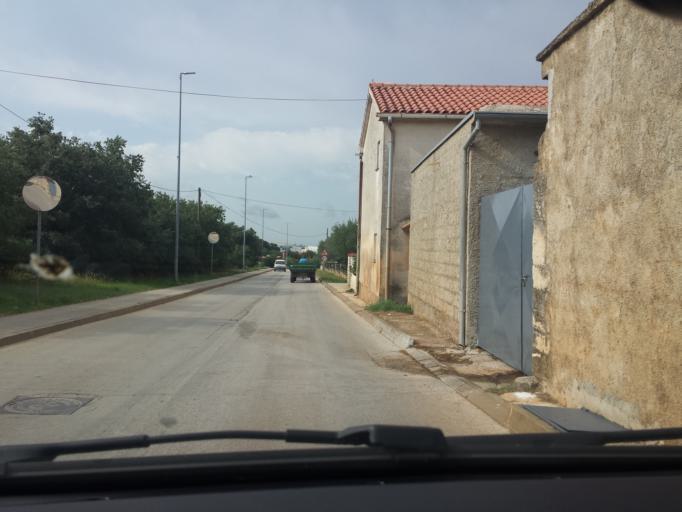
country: HR
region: Istarska
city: Galizana
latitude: 44.9267
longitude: 13.8664
